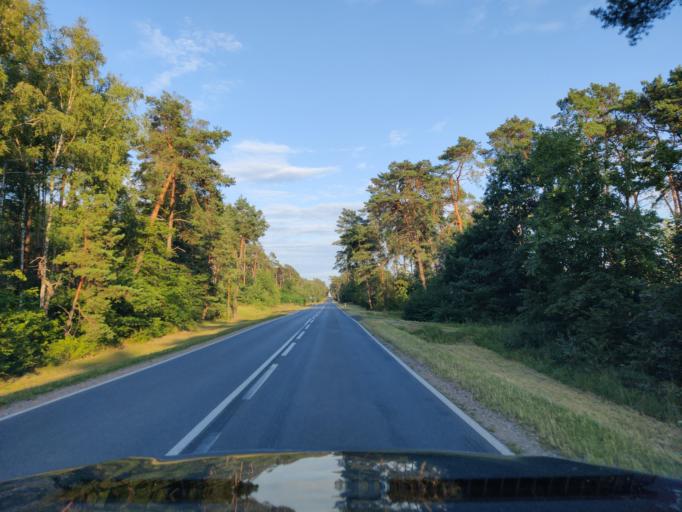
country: PL
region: Masovian Voivodeship
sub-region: Powiat pultuski
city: Pultusk
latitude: 52.6758
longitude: 21.1508
